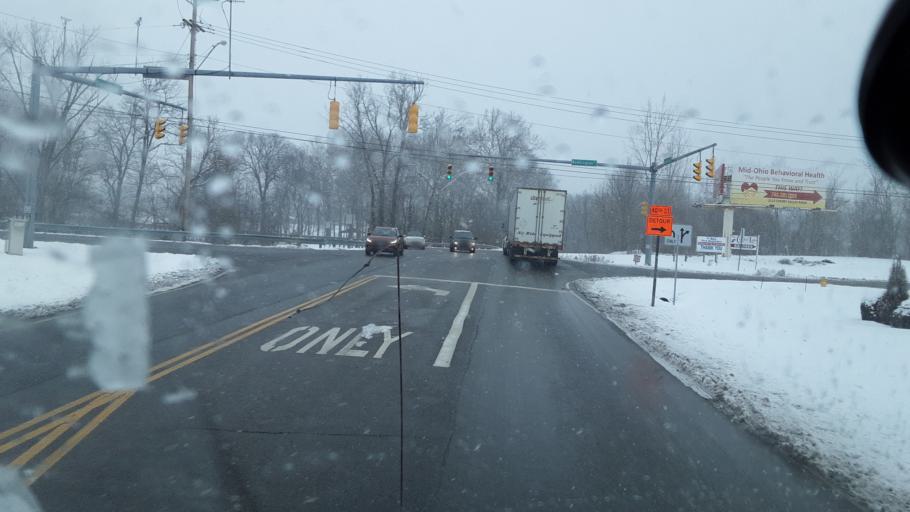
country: US
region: Ohio
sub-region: Licking County
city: Heath
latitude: 40.0466
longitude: -82.4743
